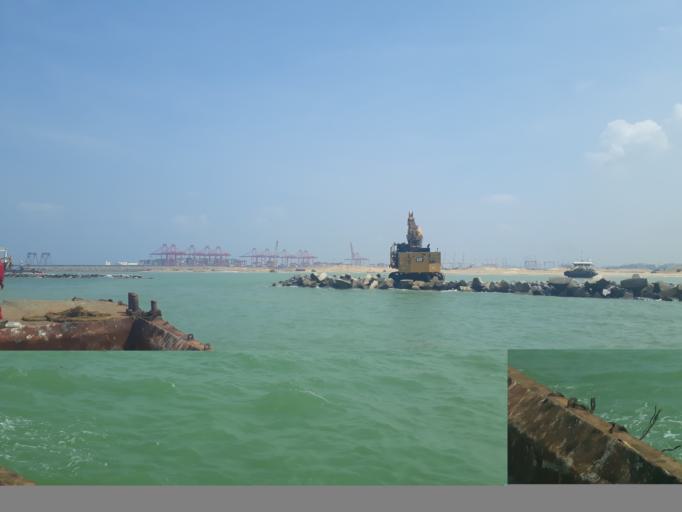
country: LK
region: Western
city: Colombo
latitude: 6.9324
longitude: 79.8200
